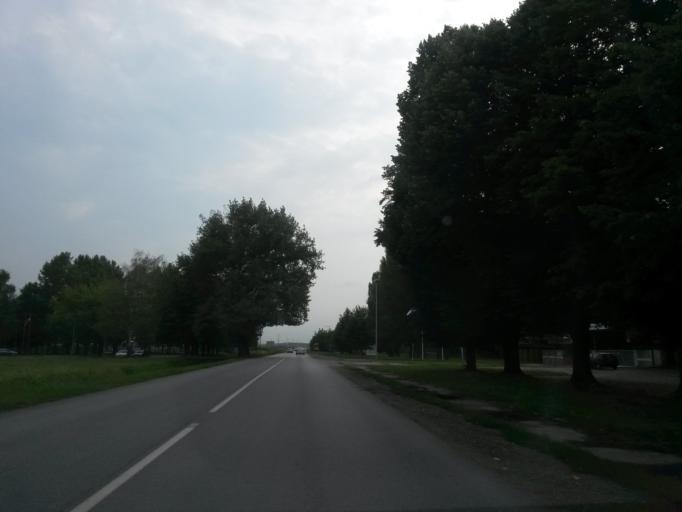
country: HR
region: Osjecko-Baranjska
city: Tenja
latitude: 45.5444
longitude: 18.7424
